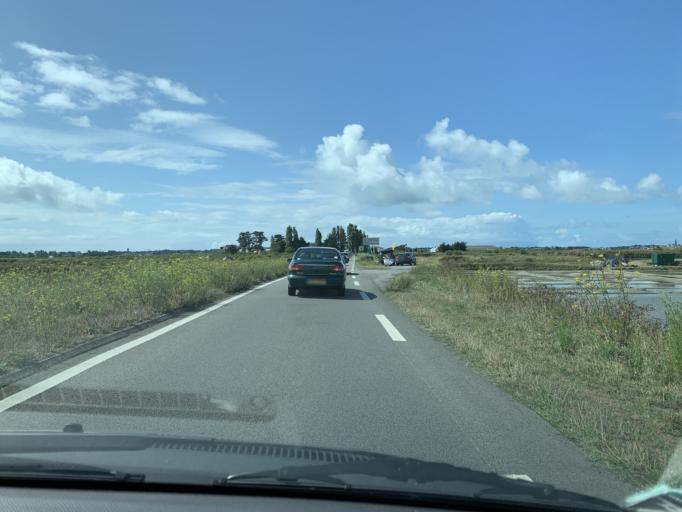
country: FR
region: Pays de la Loire
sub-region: Departement de la Loire-Atlantique
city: Le Pouliguen
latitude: 47.2938
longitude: -2.4362
